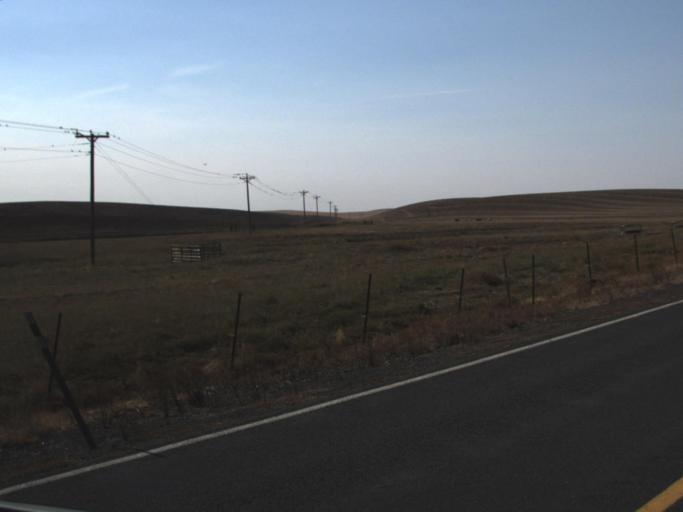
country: US
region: Washington
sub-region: Whitman County
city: Colfax
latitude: 47.1640
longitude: -117.2102
